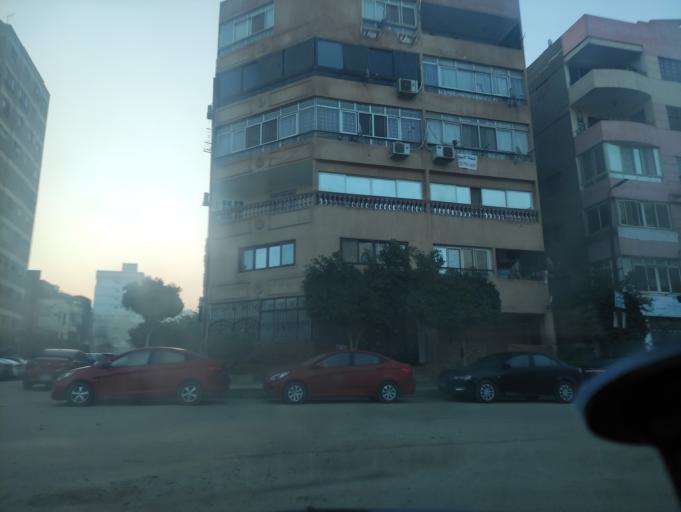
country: EG
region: Muhafazat al Qahirah
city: Cairo
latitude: 30.0511
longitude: 31.3708
